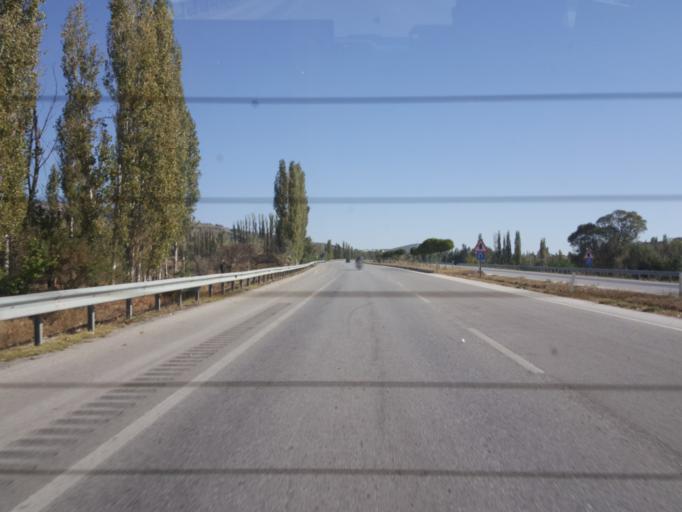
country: TR
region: Corum
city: Bogazkale
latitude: 40.2423
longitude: 34.5906
